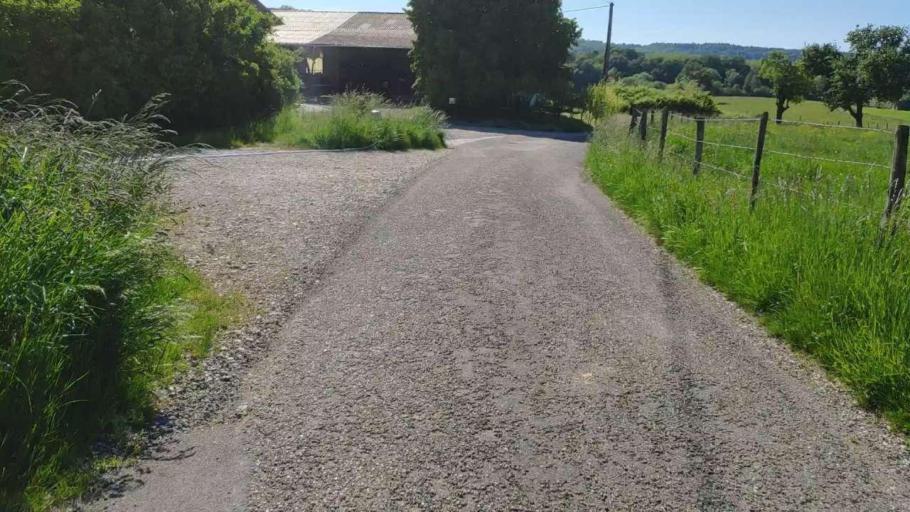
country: FR
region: Franche-Comte
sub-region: Departement du Jura
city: Perrigny
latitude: 46.7231
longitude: 5.5745
